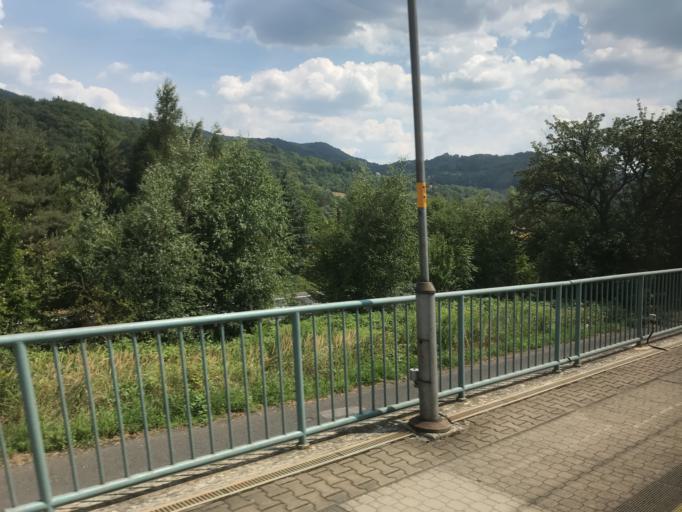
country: CZ
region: Ustecky
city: Povrly
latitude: 50.7237
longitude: 14.1860
